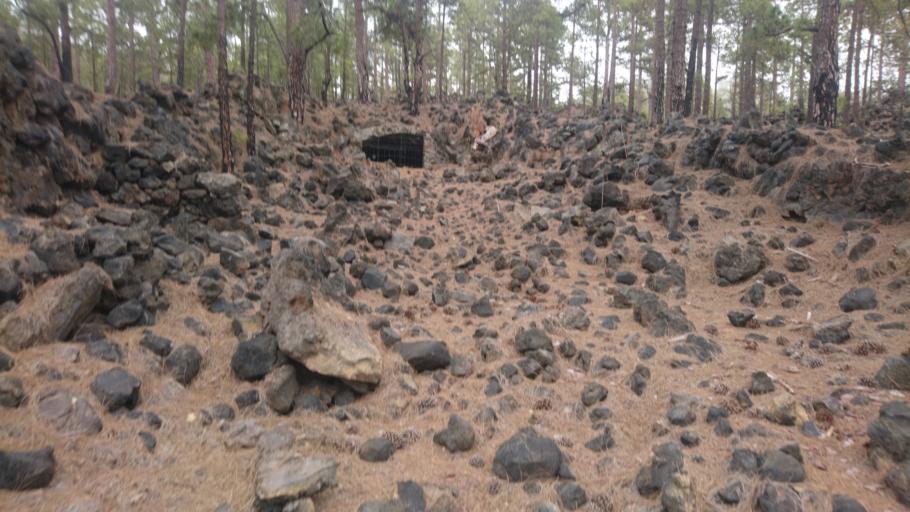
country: ES
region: Canary Islands
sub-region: Provincia de Santa Cruz de Tenerife
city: Guia de Isora
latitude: 28.2505
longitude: -16.7766
